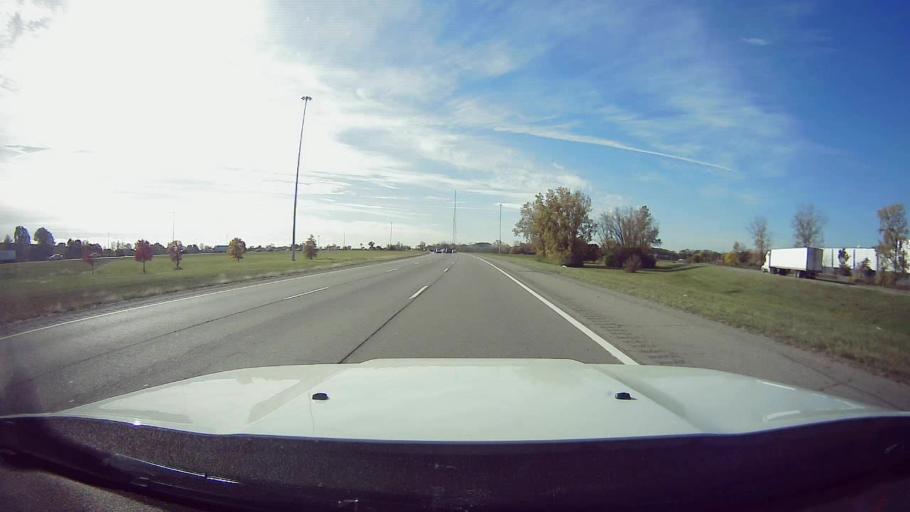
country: US
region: Michigan
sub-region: Wayne County
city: Plymouth
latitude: 42.3900
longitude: -83.4361
